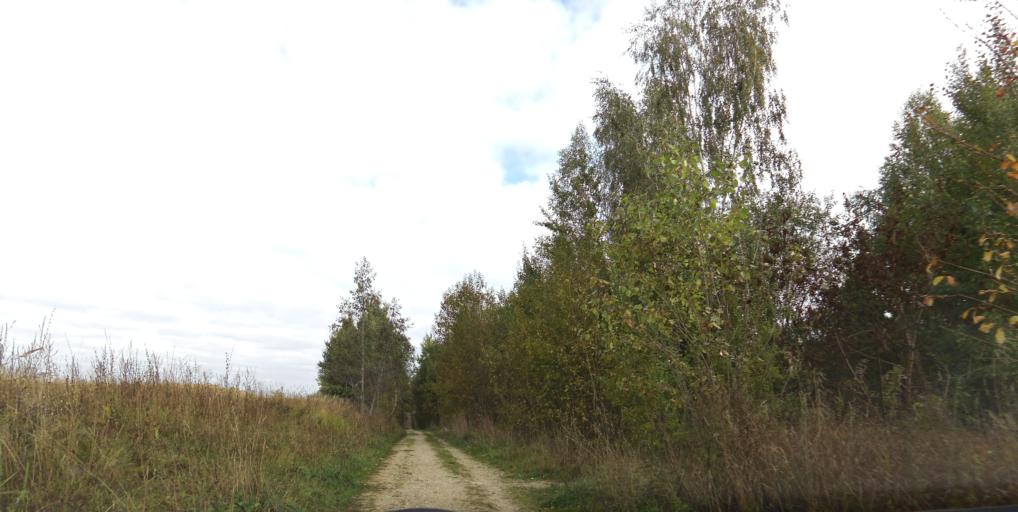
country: LT
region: Vilnius County
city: Justiniskes
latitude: 54.7142
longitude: 25.2095
